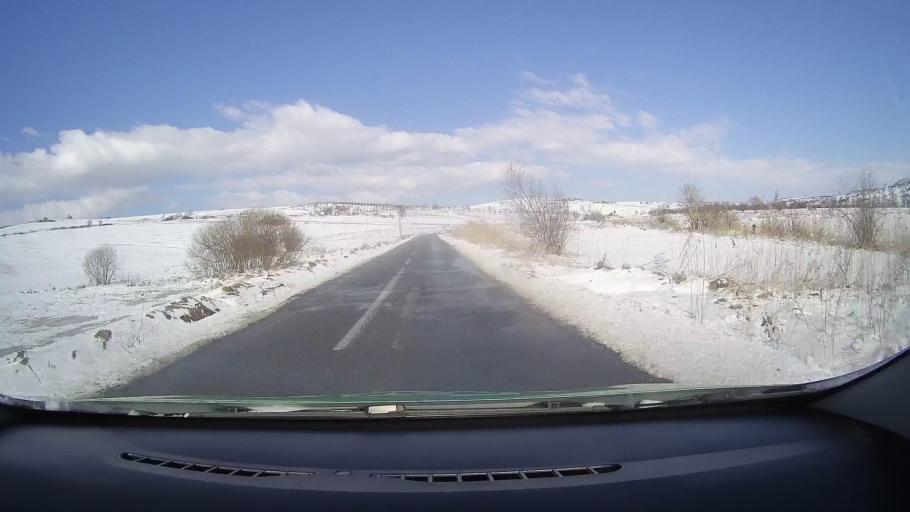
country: RO
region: Sibiu
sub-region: Comuna Vurpar
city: Vurpar
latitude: 45.8712
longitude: 24.3182
